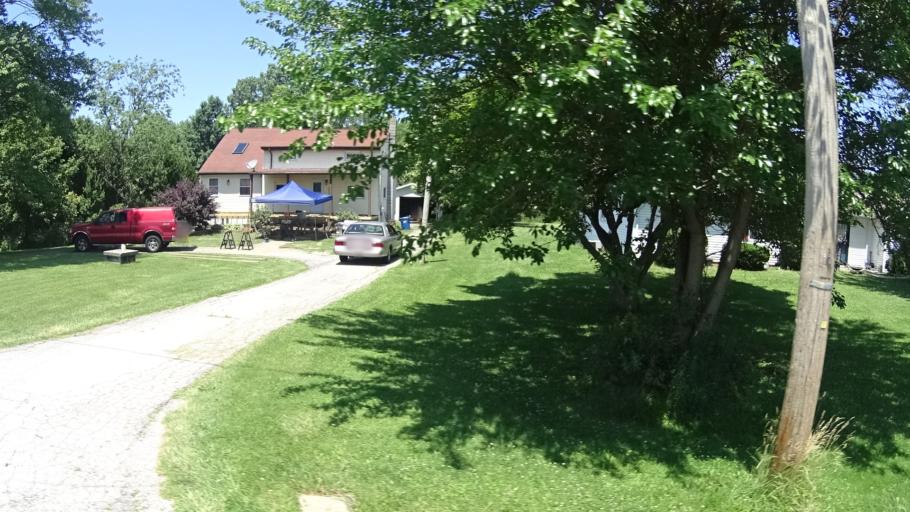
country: US
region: Ohio
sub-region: Huron County
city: Wakeman
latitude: 41.3464
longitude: -82.4273
